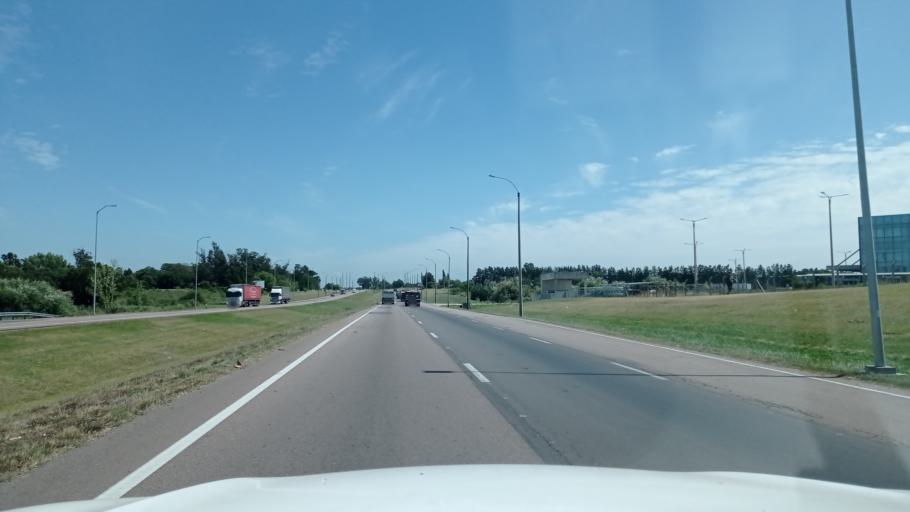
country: UY
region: Canelones
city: La Paz
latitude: -34.8059
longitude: -56.2619
